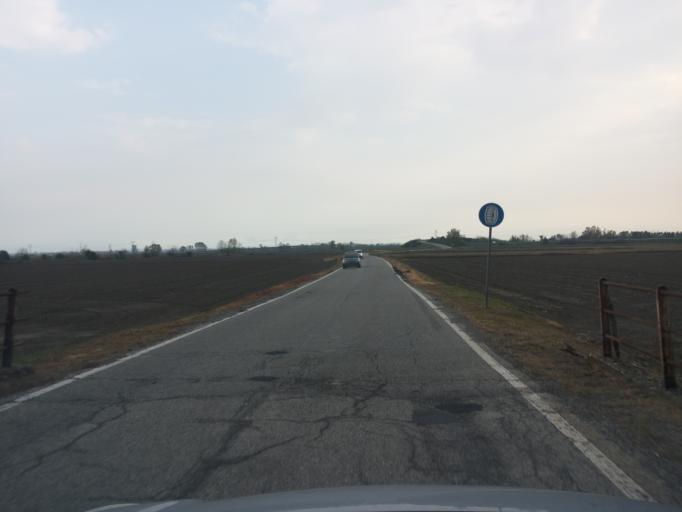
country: IT
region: Piedmont
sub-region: Provincia di Vercelli
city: Caresana
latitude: 45.1983
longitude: 8.4963
